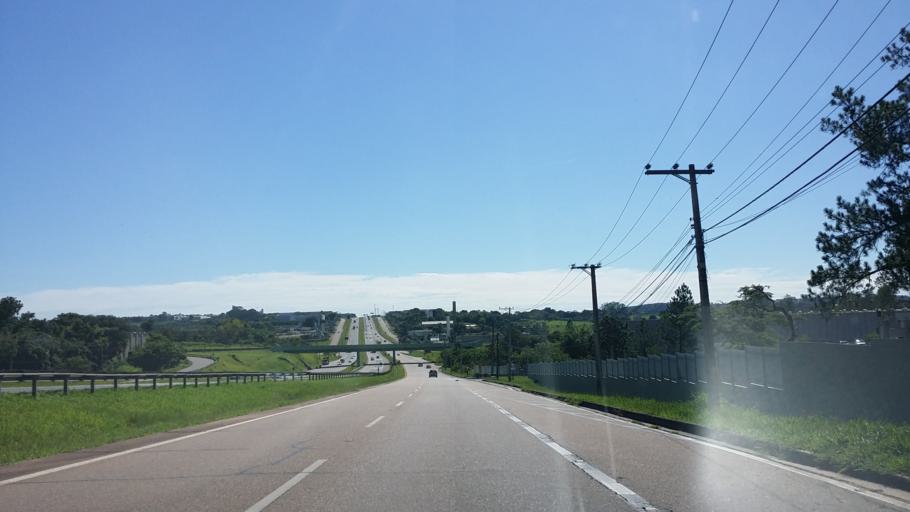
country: BR
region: Sao Paulo
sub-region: Indaiatuba
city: Indaiatuba
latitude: -23.0897
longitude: -47.1822
